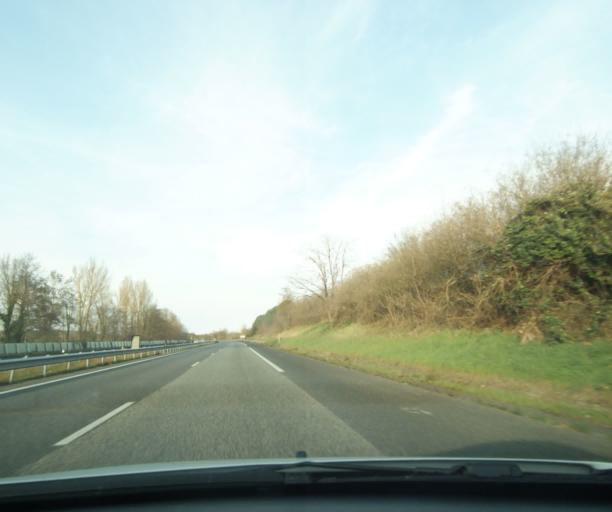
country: FR
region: Midi-Pyrenees
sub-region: Departement de la Haute-Garonne
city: Martres-Tolosane
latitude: 43.1732
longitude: 0.9754
